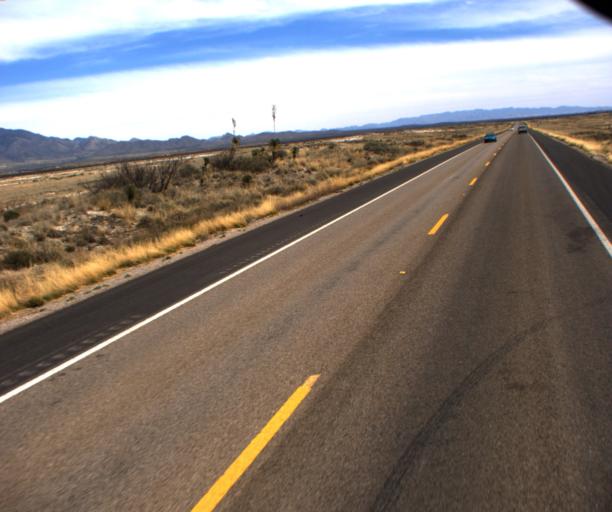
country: US
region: Arizona
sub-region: Cochise County
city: Willcox
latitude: 32.2180
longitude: -109.7866
